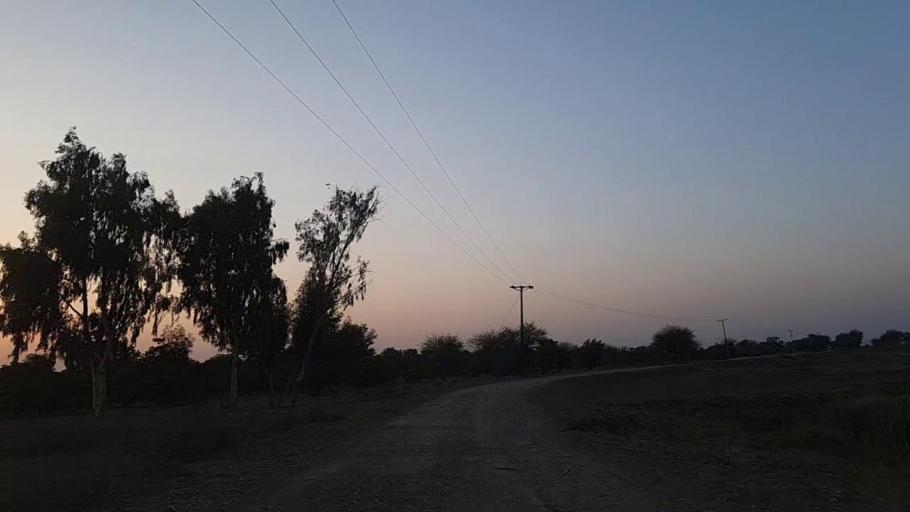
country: PK
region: Sindh
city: Naukot
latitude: 24.8878
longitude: 69.3655
